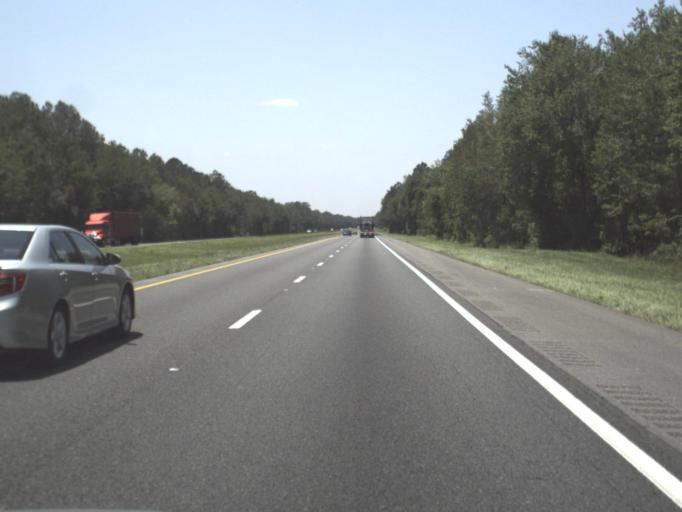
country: US
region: Florida
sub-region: Baker County
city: Macclenny
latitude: 30.2374
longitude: -82.2708
